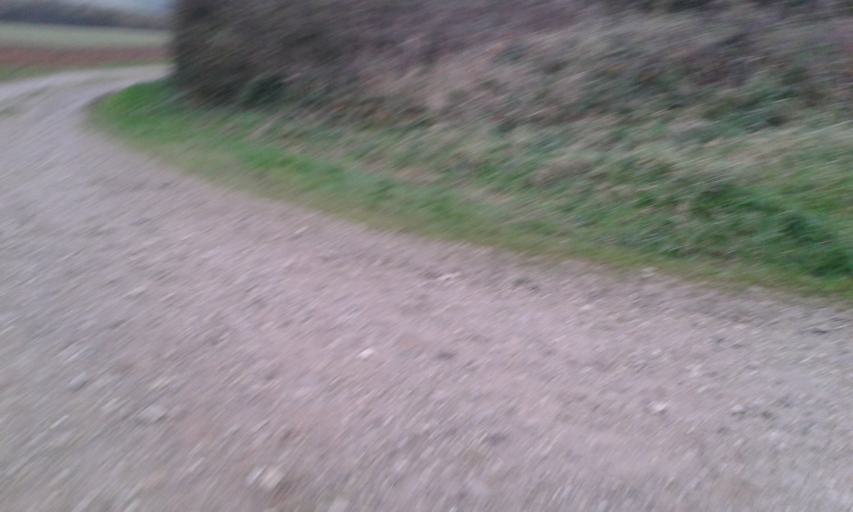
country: FR
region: Nord-Pas-de-Calais
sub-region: Departement du Pas-de-Calais
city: Marquise
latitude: 50.8659
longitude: 1.7179
